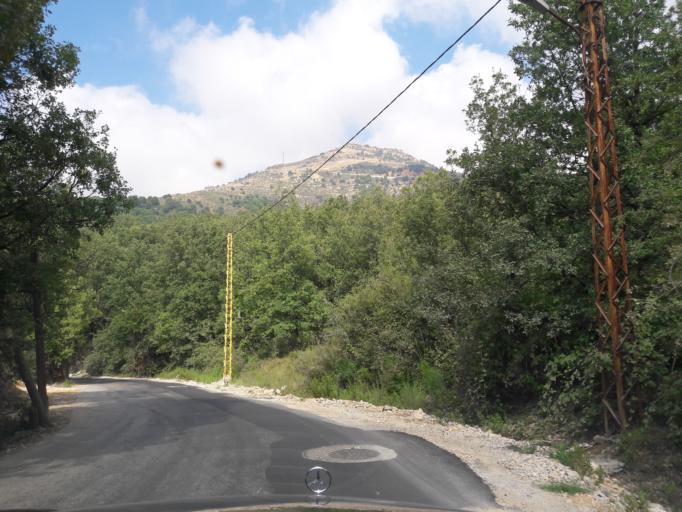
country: LB
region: Mont-Liban
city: Djounie
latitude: 33.9525
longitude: 35.7763
